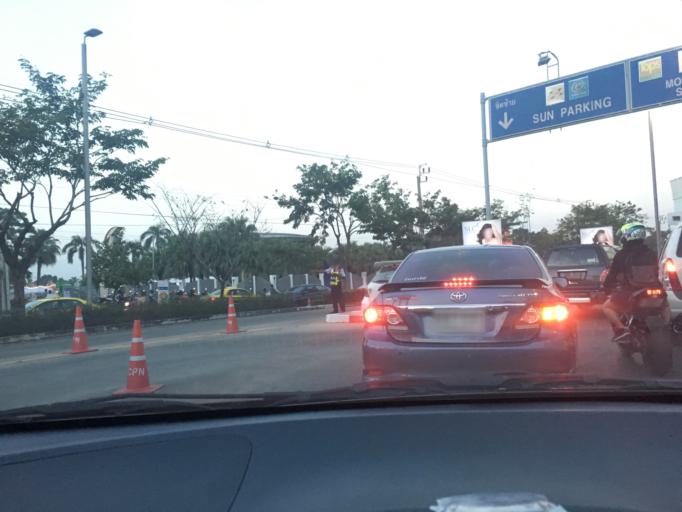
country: TH
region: Bangkok
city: Bang Khun Thian
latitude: 13.6636
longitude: 100.4364
